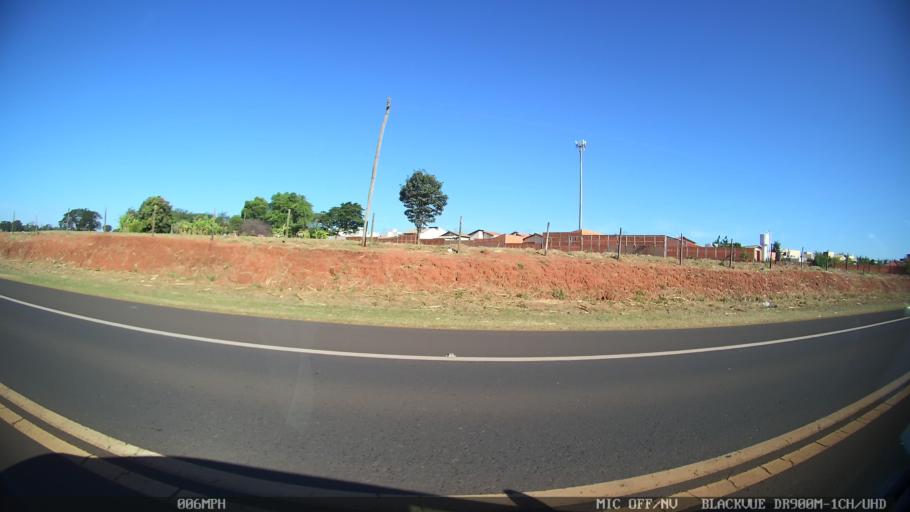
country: BR
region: Sao Paulo
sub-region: Olimpia
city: Olimpia
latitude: -20.7375
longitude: -48.8817
